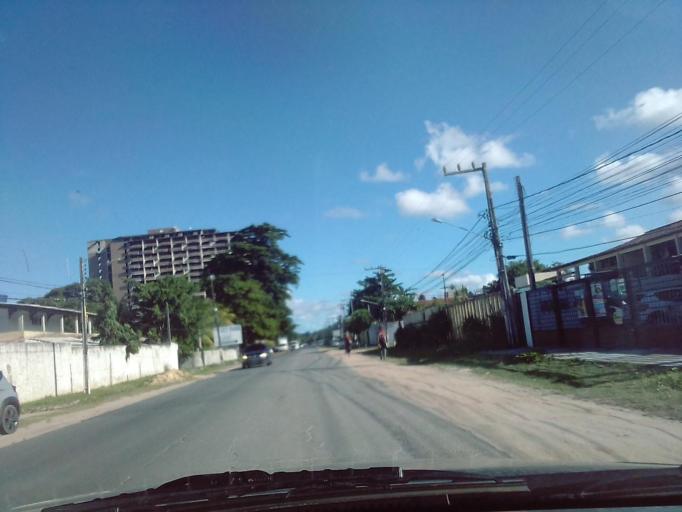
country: BR
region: Pernambuco
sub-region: Igarassu
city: Igarassu
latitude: -7.8603
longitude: -34.8360
